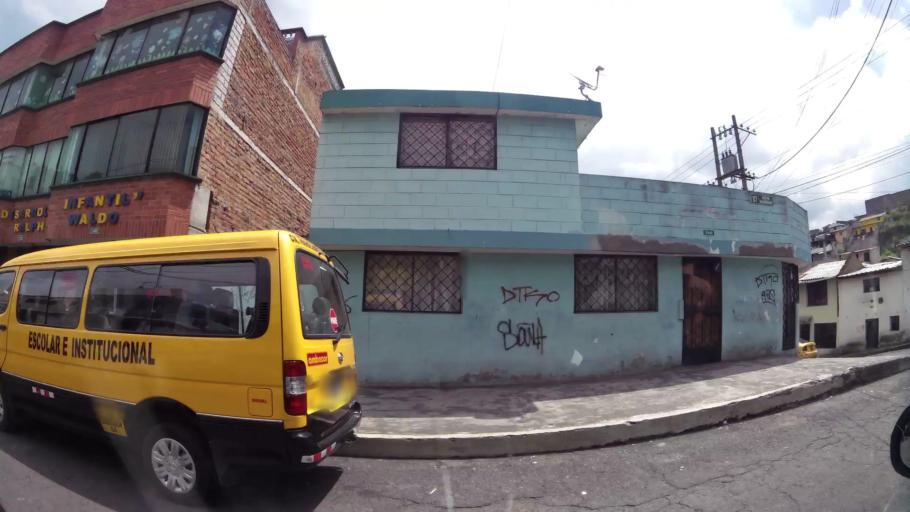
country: EC
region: Pichincha
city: Quito
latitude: -0.2541
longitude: -78.5109
